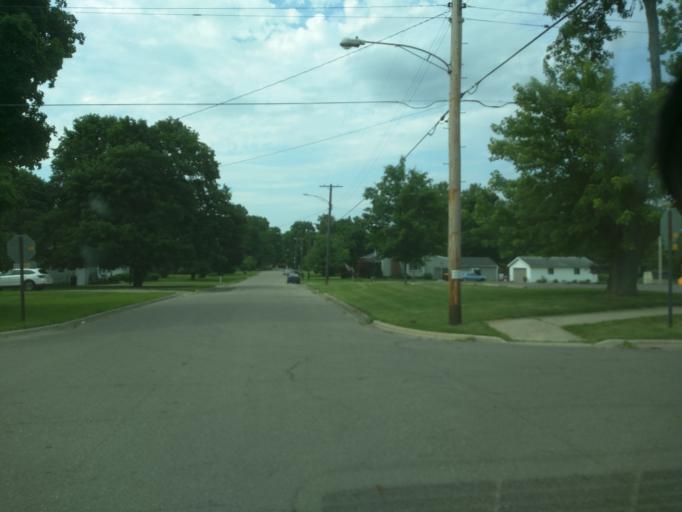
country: US
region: Michigan
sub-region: Eaton County
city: Waverly
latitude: 42.7446
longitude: -84.6151
